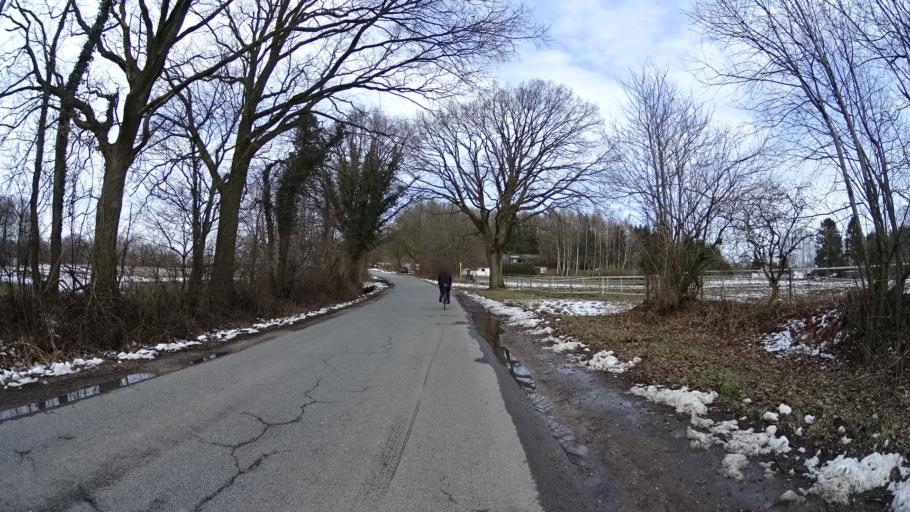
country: DE
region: Schleswig-Holstein
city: Loptin
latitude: 54.1928
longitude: 10.2306
